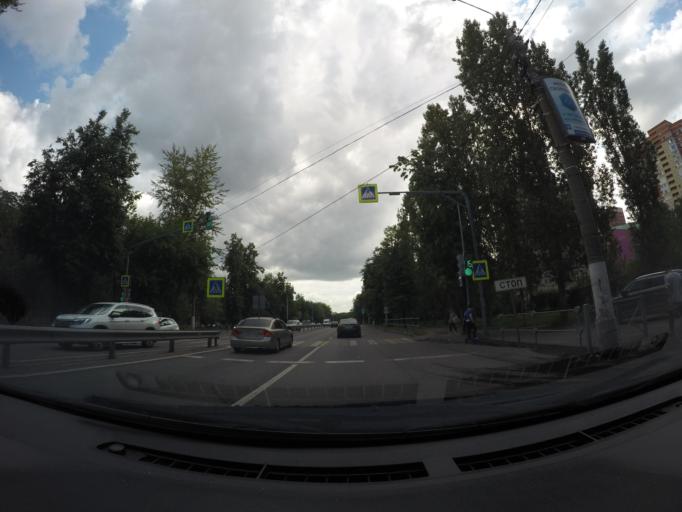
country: RU
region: Moscow
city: Zhulebino
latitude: 55.6909
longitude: 37.8685
